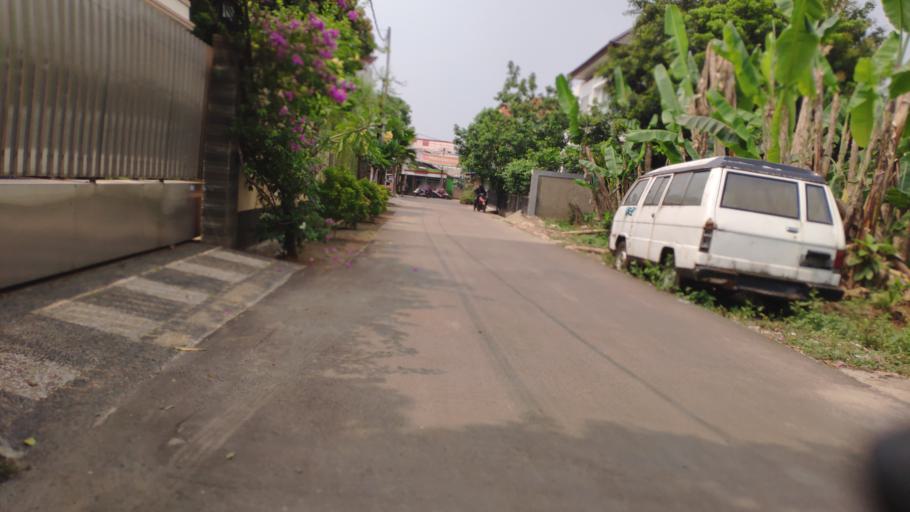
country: ID
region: West Java
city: Depok
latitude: -6.3688
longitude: 106.8053
